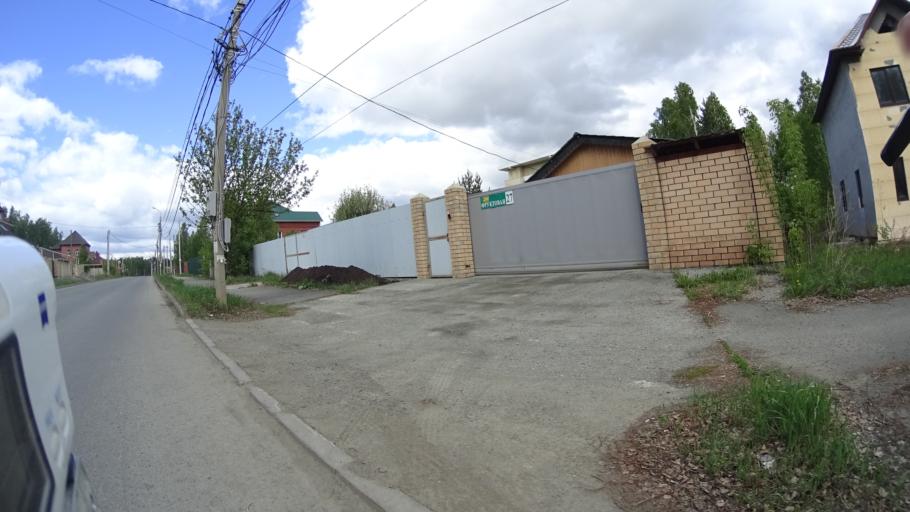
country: RU
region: Chelyabinsk
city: Sargazy
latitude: 55.1583
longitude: 61.2519
